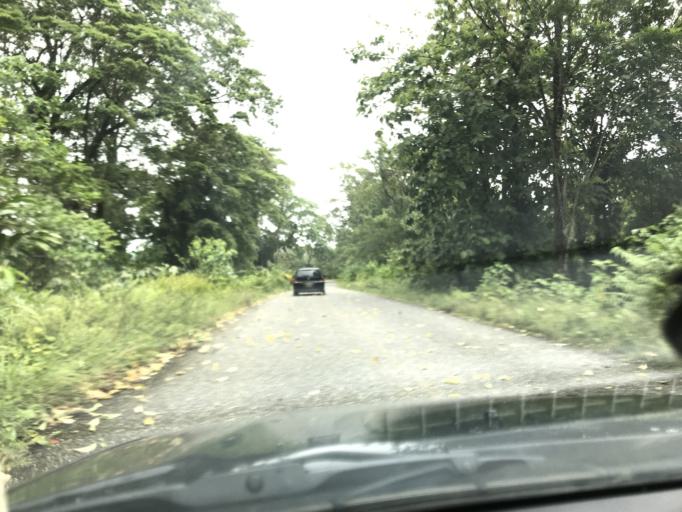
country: SB
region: Western Province
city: Gizo
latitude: -8.2328
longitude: 157.2121
